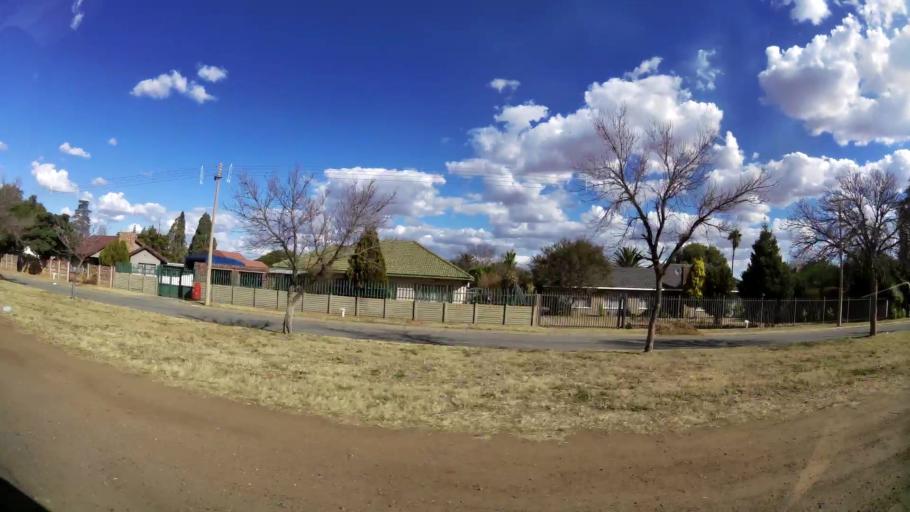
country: ZA
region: North-West
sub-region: Dr Kenneth Kaunda District Municipality
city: Klerksdorp
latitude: -26.8424
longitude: 26.6541
